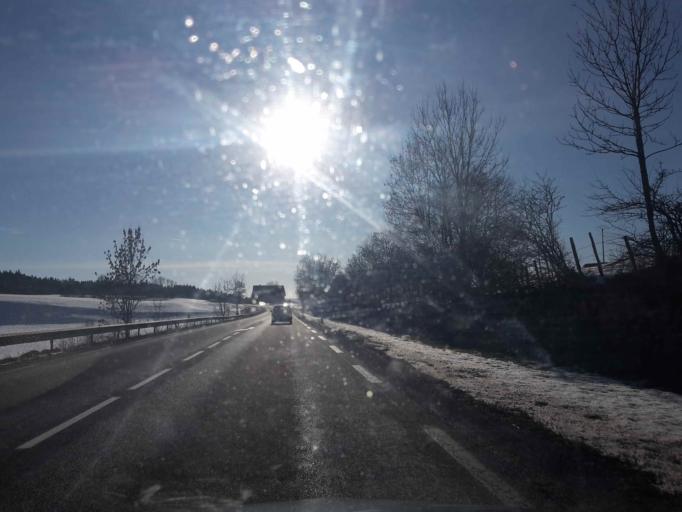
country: FR
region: Franche-Comte
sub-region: Departement du Doubs
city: Doubs
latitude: 47.0366
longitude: 6.3382
